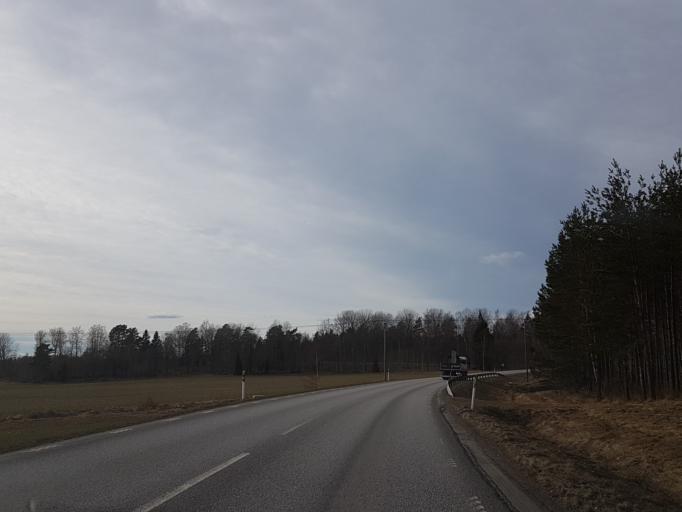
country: SE
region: Stockholm
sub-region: Norrtalje Kommun
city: Norrtalje
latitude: 59.6882
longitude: 18.6675
